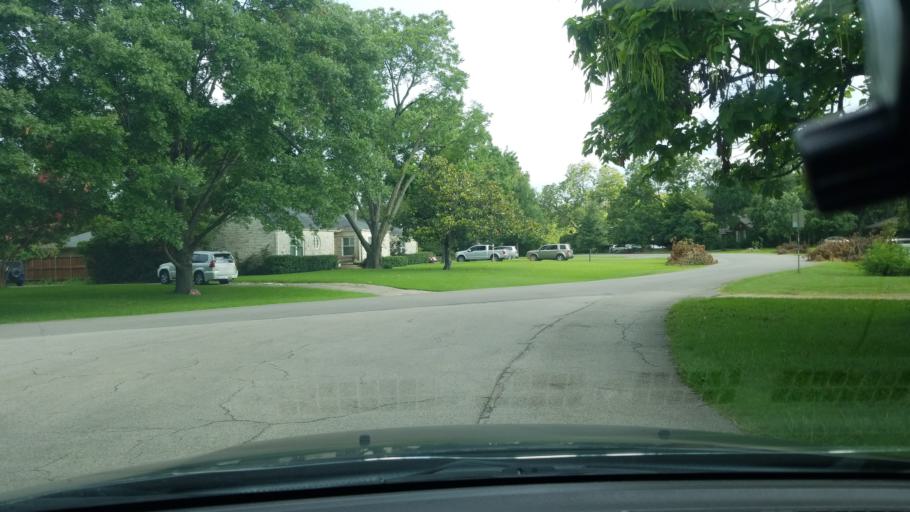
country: US
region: Texas
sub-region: Dallas County
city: Highland Park
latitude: 32.8273
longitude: -96.6950
